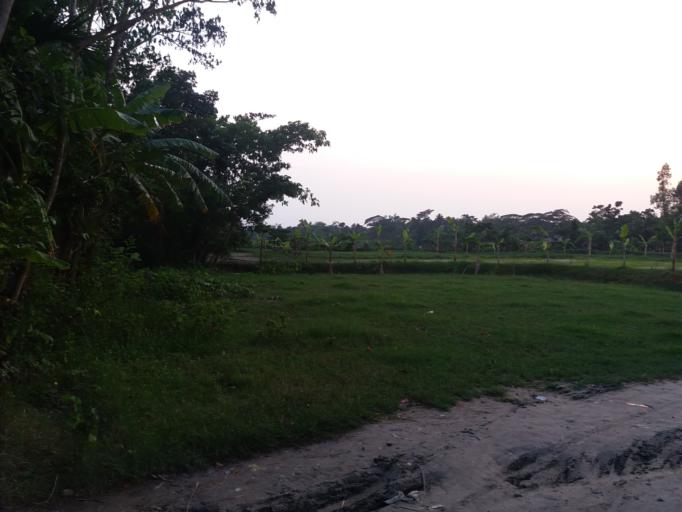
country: BD
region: Chittagong
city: Feni
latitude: 22.9346
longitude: 91.3477
